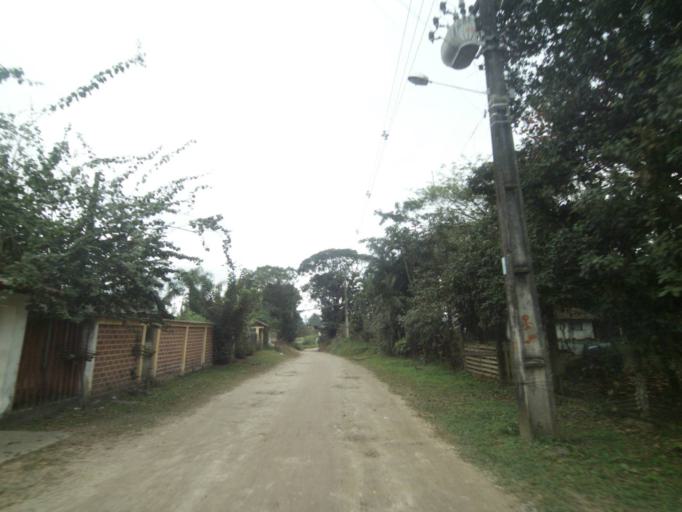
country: BR
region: Parana
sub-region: Paranagua
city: Paranagua
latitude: -25.5417
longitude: -48.5552
